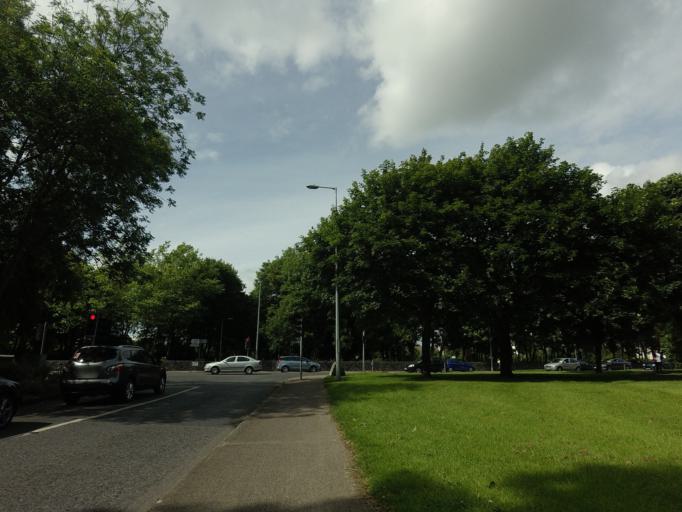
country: IE
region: Leinster
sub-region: Fingal County
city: Blanchardstown
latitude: 53.3829
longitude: -6.3932
